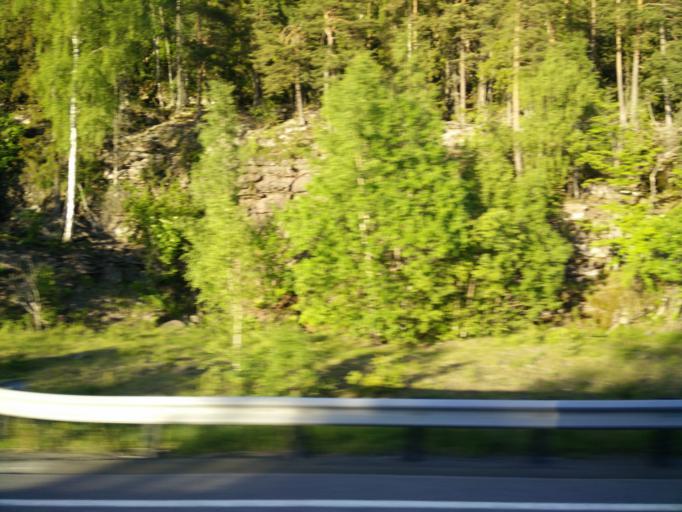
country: NO
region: Buskerud
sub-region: Hole
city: Vik
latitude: 60.0194
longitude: 10.2681
